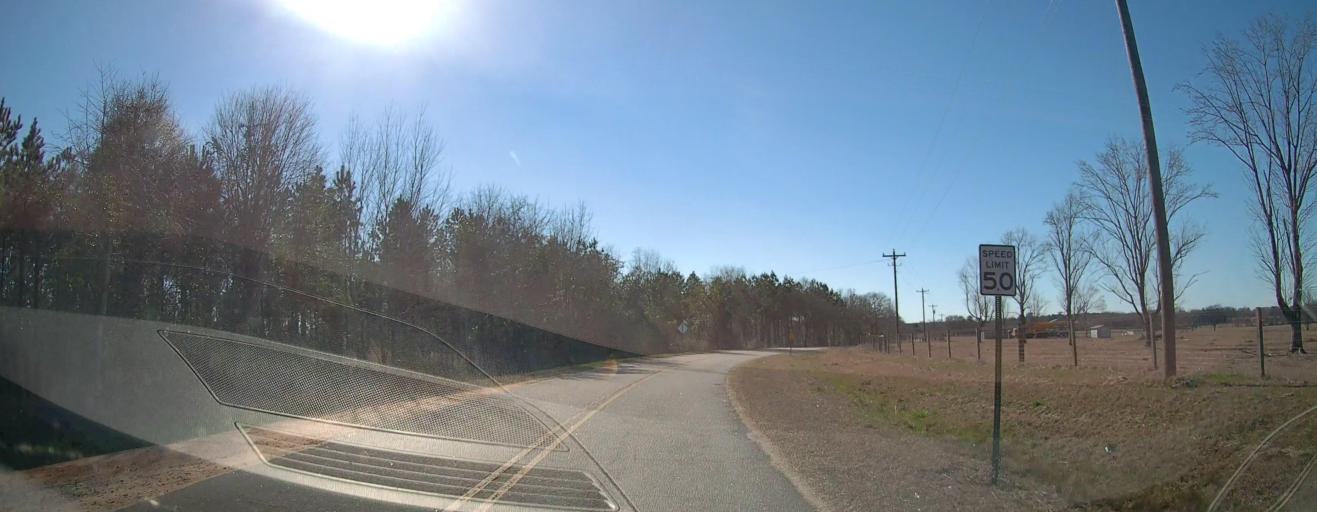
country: US
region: Georgia
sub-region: Taylor County
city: Butler
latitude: 32.6249
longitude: -84.2513
